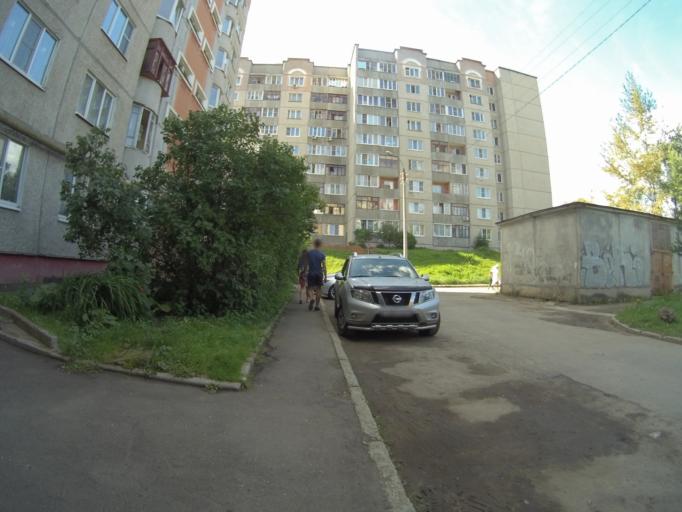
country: RU
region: Vladimir
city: Vladimir
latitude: 56.1375
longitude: 40.3703
